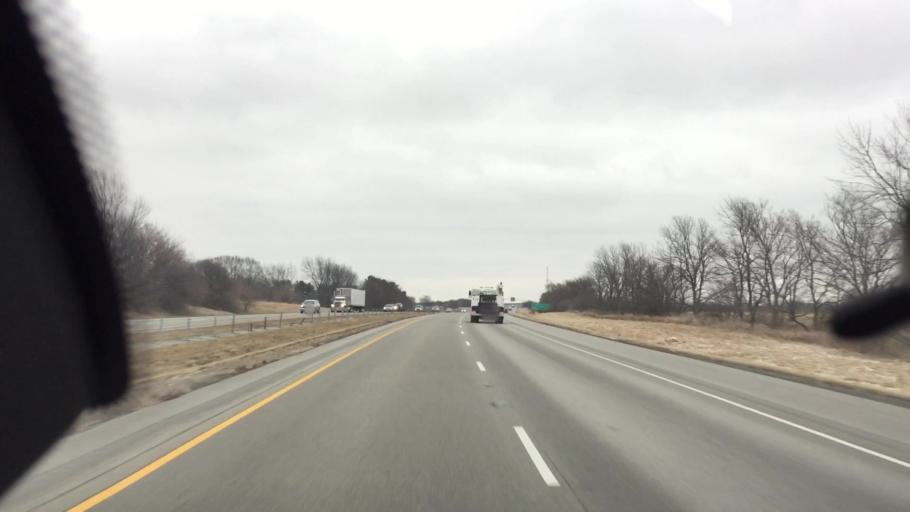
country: US
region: Illinois
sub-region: Champaign County
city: Lake of the Woods
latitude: 40.1670
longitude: -88.3086
